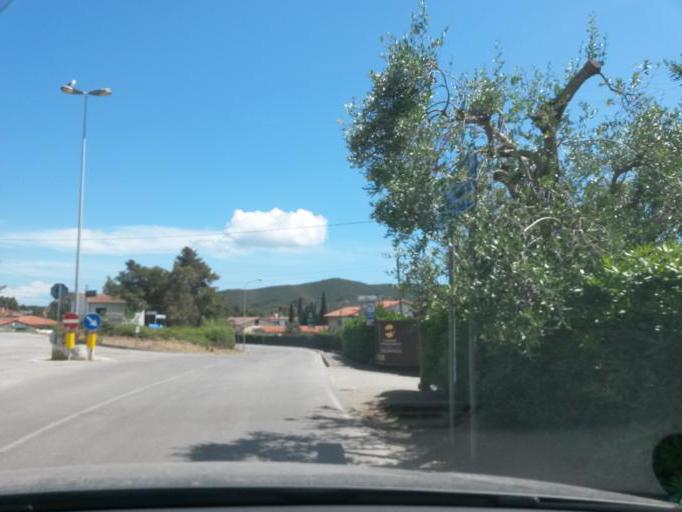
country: IT
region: Tuscany
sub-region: Provincia di Livorno
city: Portoferraio
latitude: 42.7621
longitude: 10.2993
